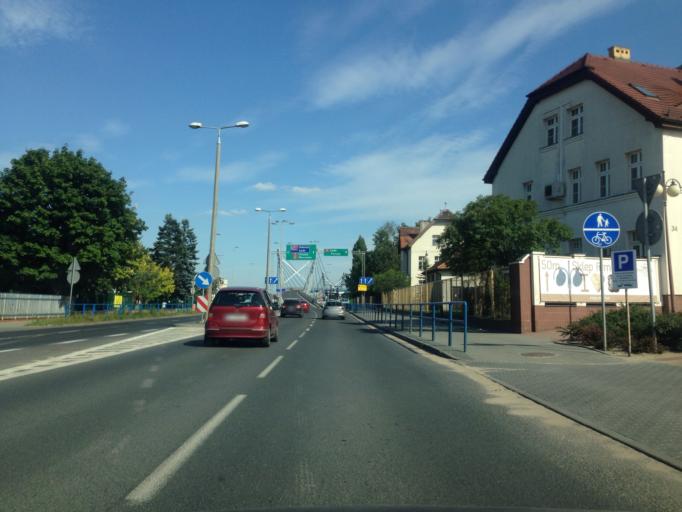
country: PL
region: Kujawsko-Pomorskie
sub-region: Torun
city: Torun
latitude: 53.0228
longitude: 18.6419
